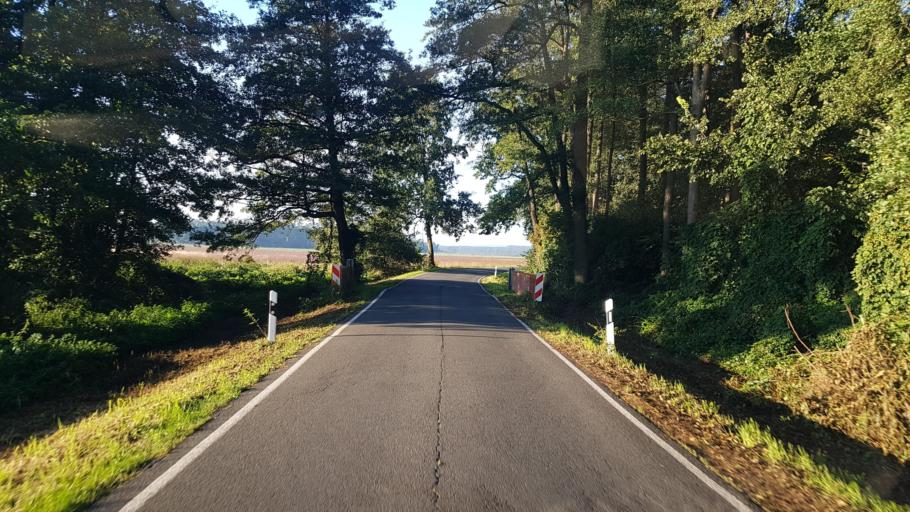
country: DE
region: Saxony-Anhalt
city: Holzdorf
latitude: 51.8242
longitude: 13.1039
